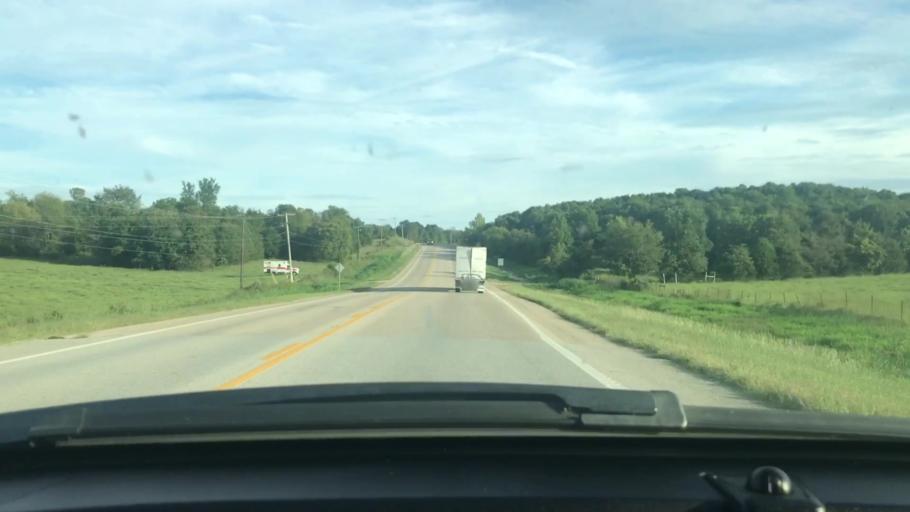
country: US
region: Arkansas
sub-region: Randolph County
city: Pocahontas
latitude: 36.1926
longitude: -91.1657
